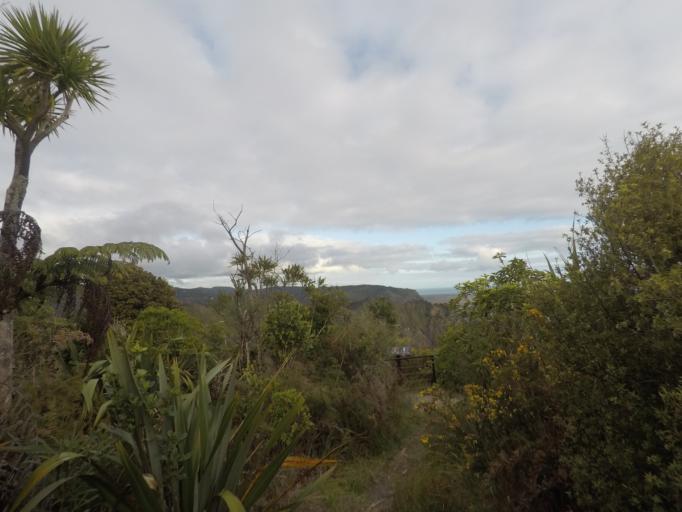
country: NZ
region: Auckland
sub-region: Auckland
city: Muriwai Beach
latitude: -36.9721
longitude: 174.4668
